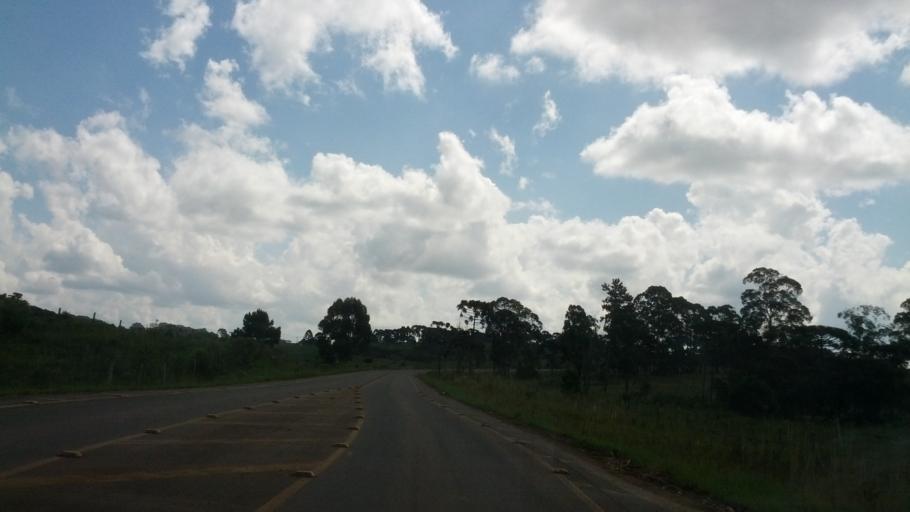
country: BR
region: Rio Grande do Sul
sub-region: Vacaria
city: Estrela
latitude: -27.7977
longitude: -50.8788
